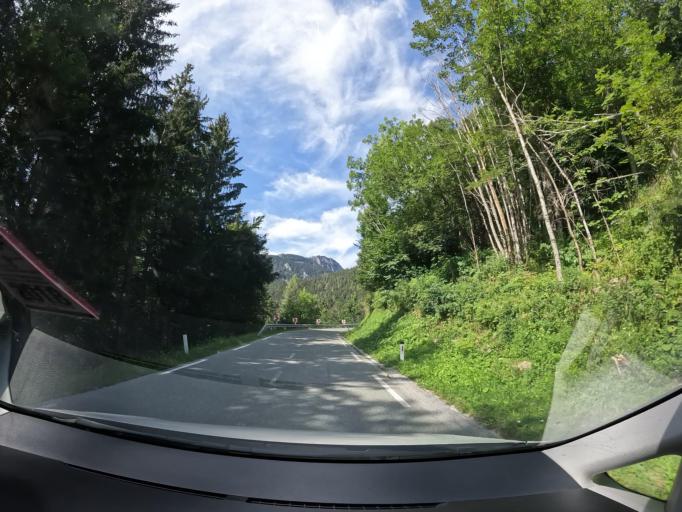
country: AT
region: Carinthia
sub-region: Politischer Bezirk Sankt Veit an der Glan
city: Liebenfels
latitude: 46.7164
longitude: 14.2552
